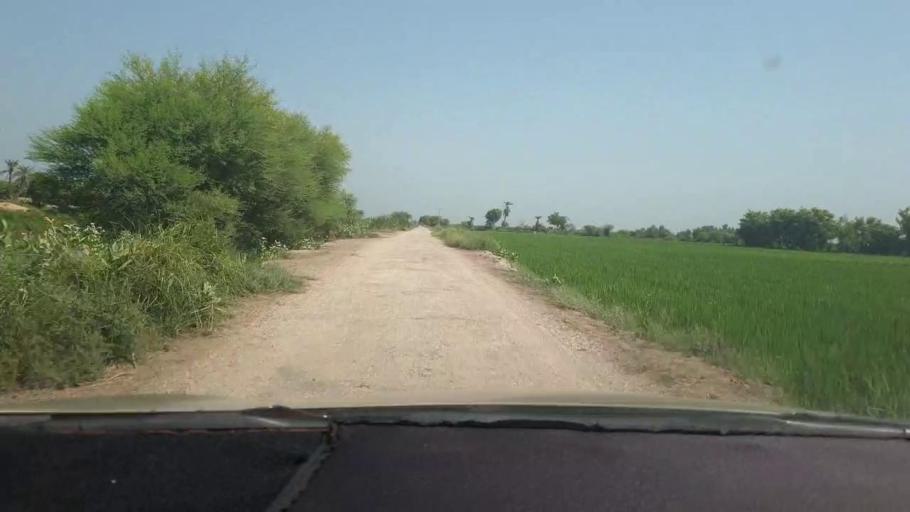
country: PK
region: Sindh
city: Miro Khan
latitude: 27.6947
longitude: 68.0996
